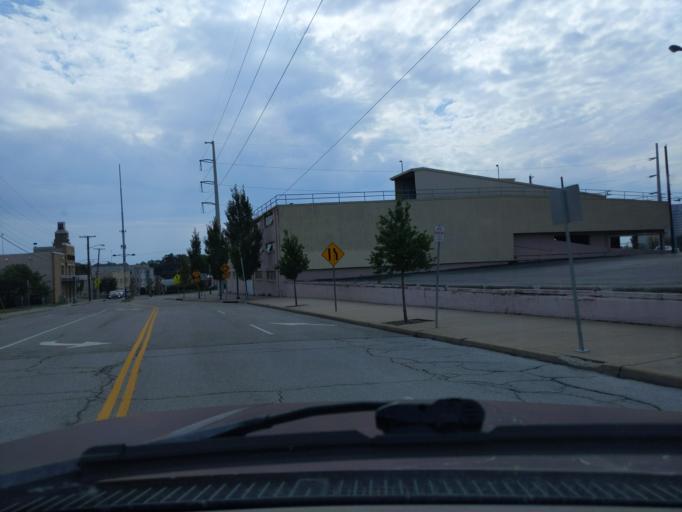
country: US
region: Oklahoma
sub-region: Tulsa County
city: Tulsa
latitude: 36.1492
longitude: -95.9833
